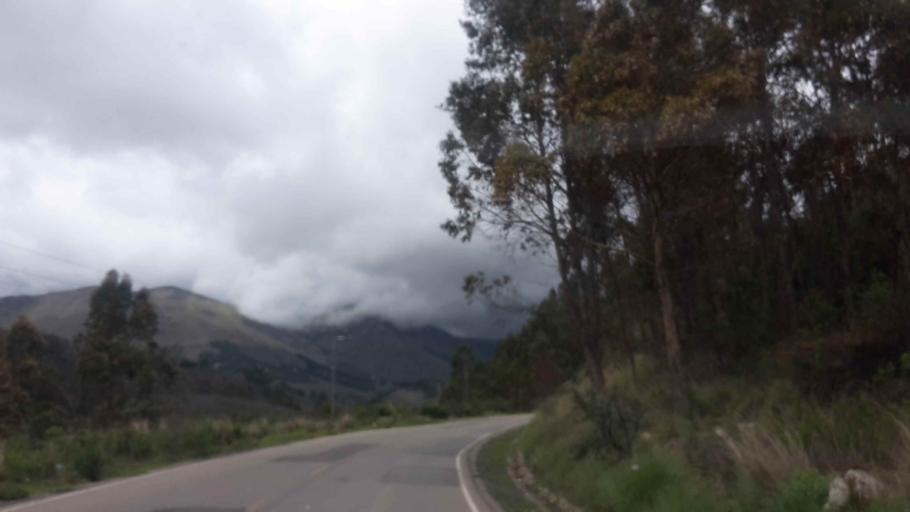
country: BO
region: Cochabamba
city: Arani
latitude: -17.4772
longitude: -65.5311
